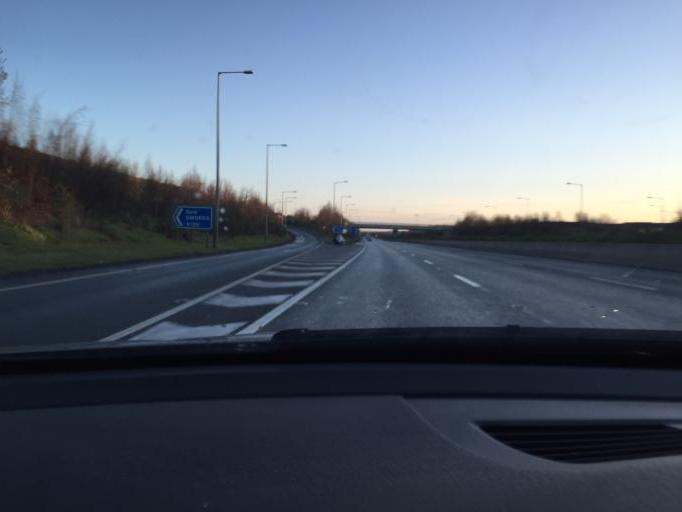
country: IE
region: Leinster
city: Kinsealy-Drinan
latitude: 53.4402
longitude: -6.2078
